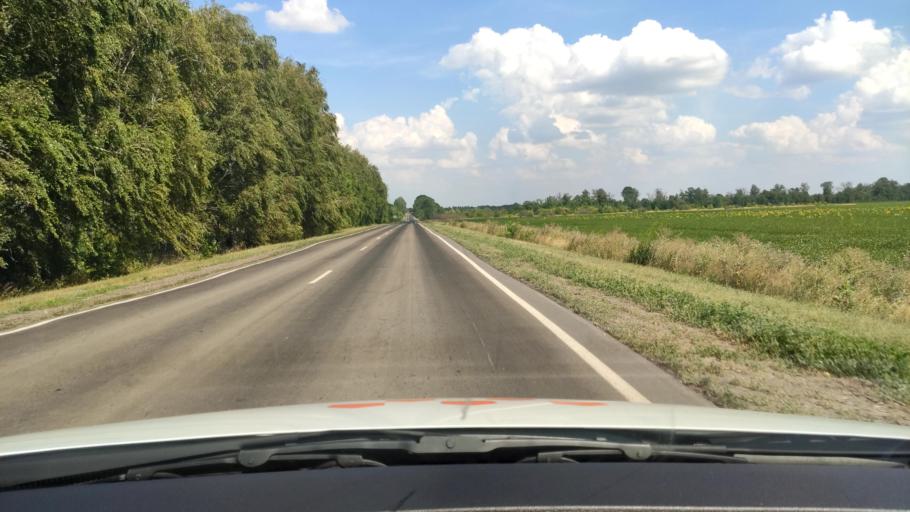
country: RU
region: Voronezj
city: Ertil'
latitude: 51.8099
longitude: 40.7964
